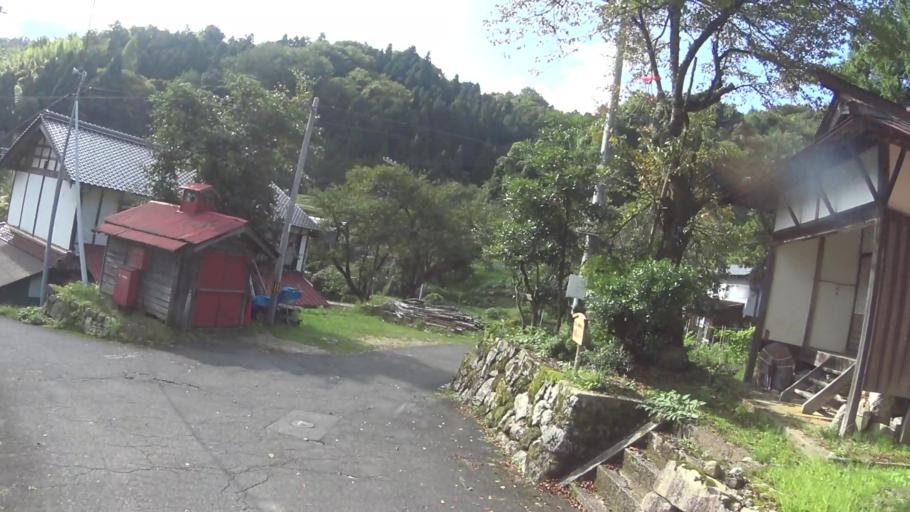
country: JP
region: Kyoto
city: Miyazu
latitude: 35.6112
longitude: 135.1962
